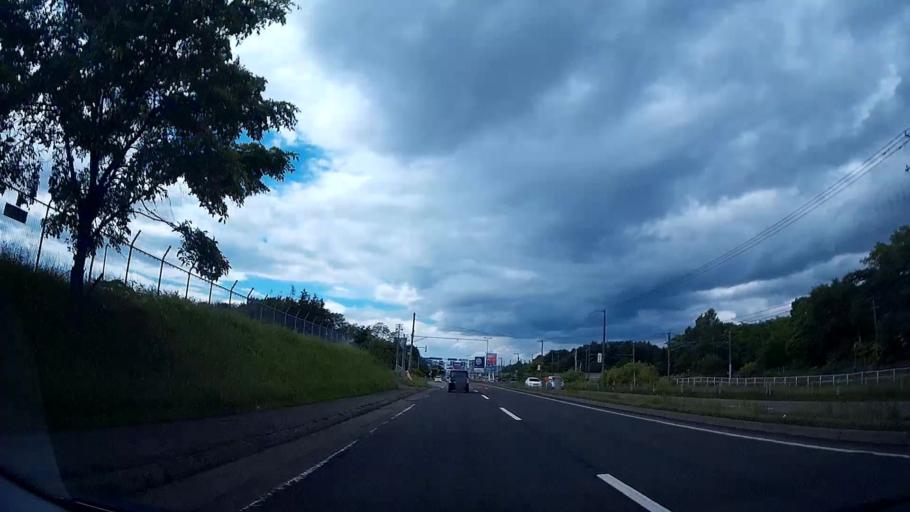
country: JP
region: Hokkaido
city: Chitose
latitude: 42.8175
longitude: 141.6637
